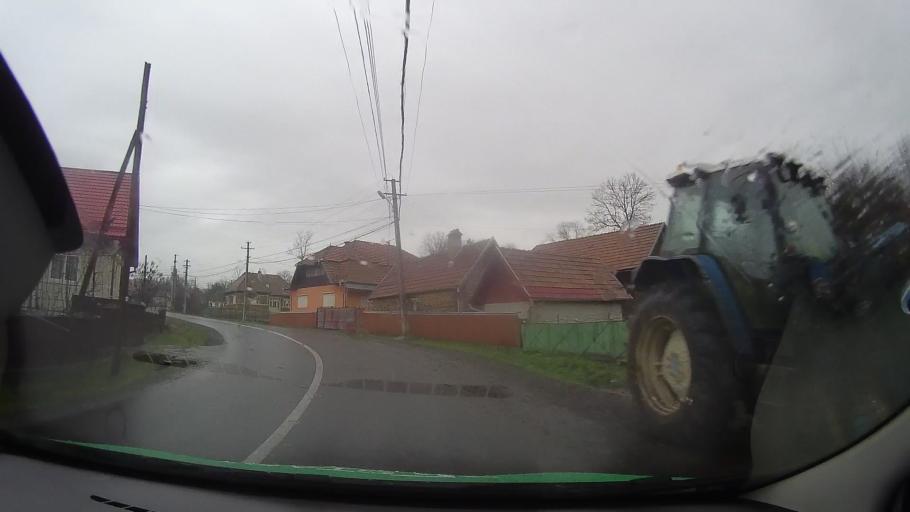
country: RO
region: Mures
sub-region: Comuna Vatava
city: Vatava
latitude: 46.9565
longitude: 24.7632
